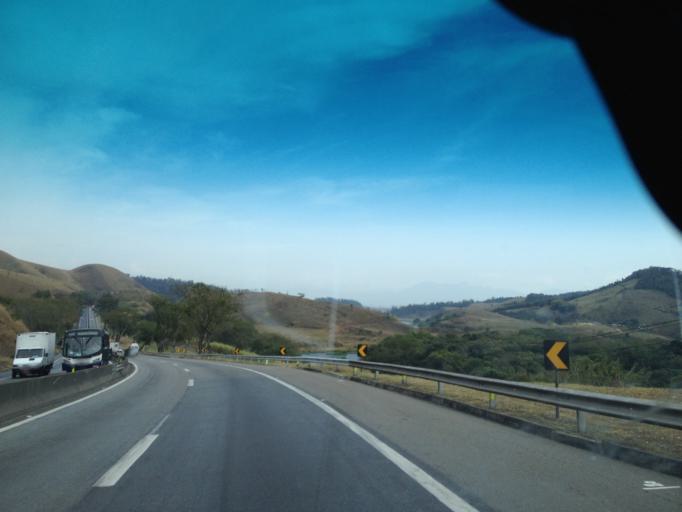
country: BR
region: Rio de Janeiro
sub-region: Porto Real
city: Porto Real
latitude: -22.4759
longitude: -44.2653
